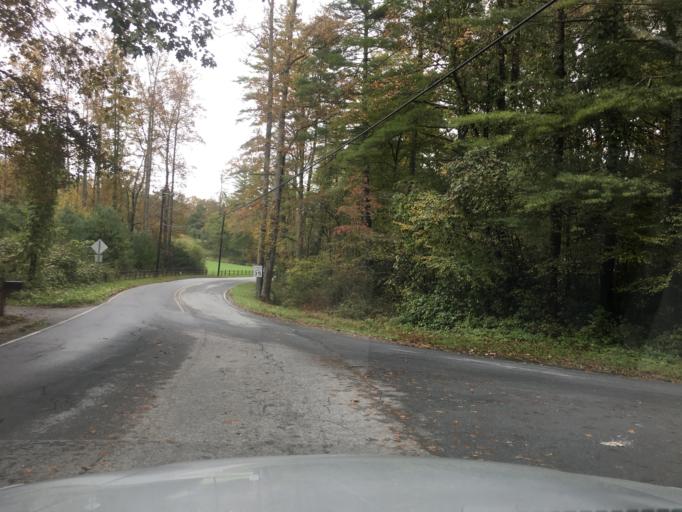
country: US
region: North Carolina
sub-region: Henderson County
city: Valley Hill
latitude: 35.2969
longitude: -82.4904
